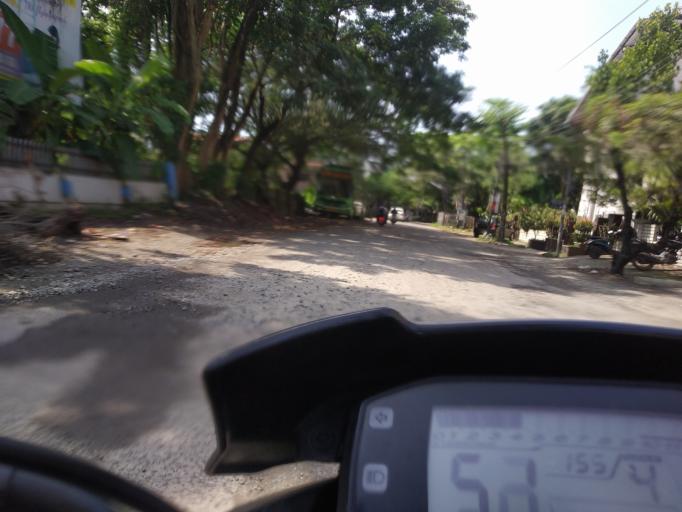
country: IN
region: Kerala
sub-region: Ernakulam
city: Cochin
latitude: 9.9748
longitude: 76.2954
